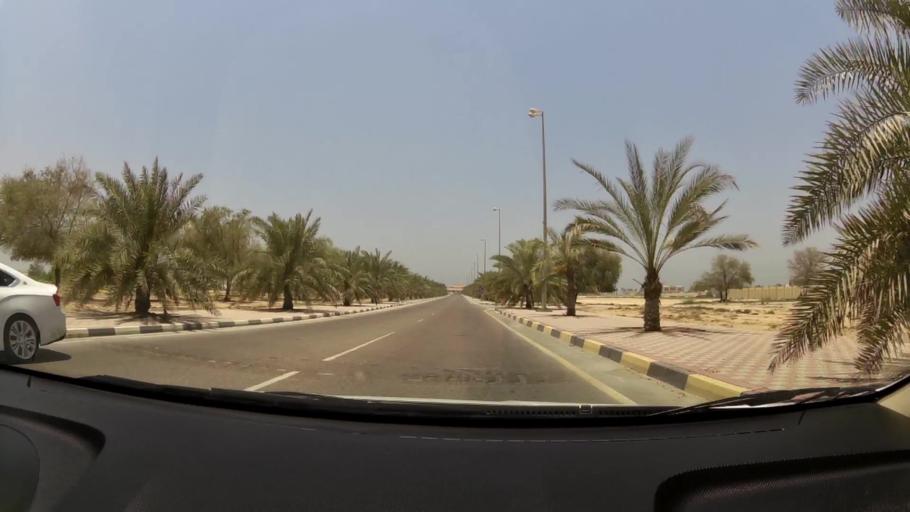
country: AE
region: Umm al Qaywayn
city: Umm al Qaywayn
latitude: 25.5298
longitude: 55.5351
